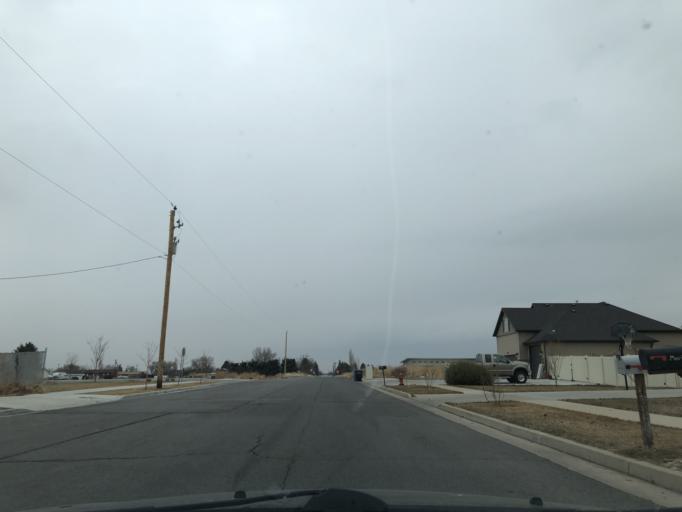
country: US
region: Utah
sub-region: Cache County
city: Nibley
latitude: 41.6906
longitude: -111.8622
